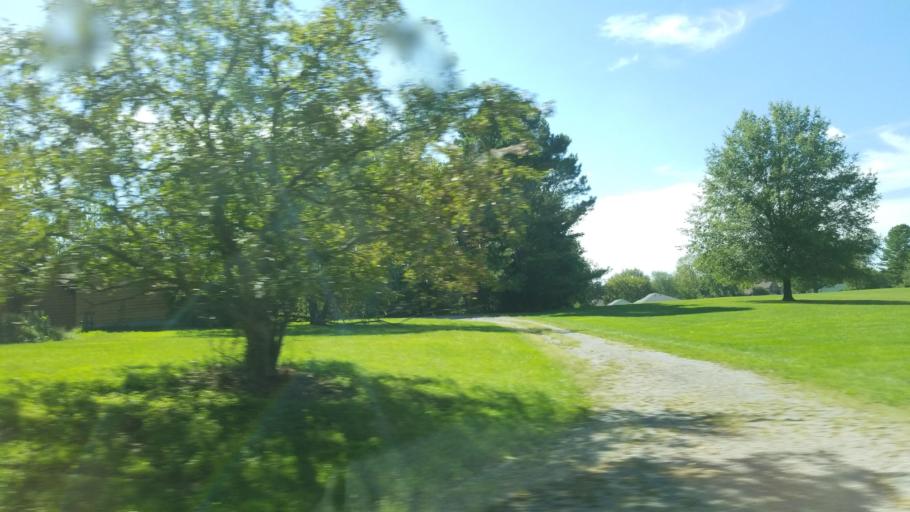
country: US
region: Illinois
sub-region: Williamson County
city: Marion
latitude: 37.7474
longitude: -88.8785
